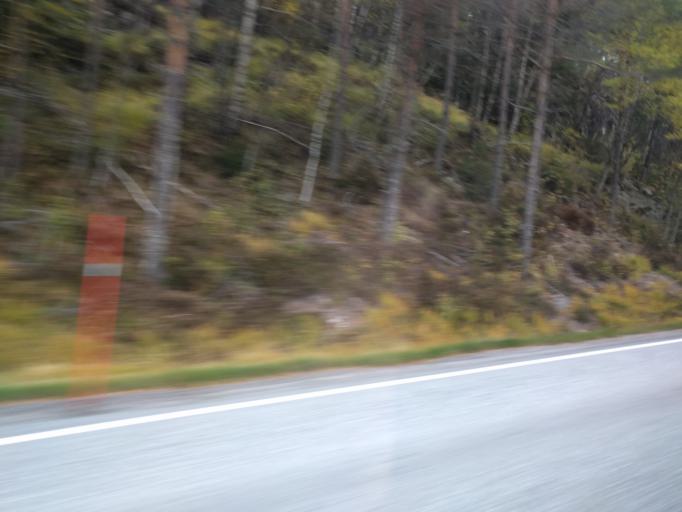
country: NO
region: Aust-Agder
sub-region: Iveland
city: Birketveit
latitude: 58.3755
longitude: 7.7623
